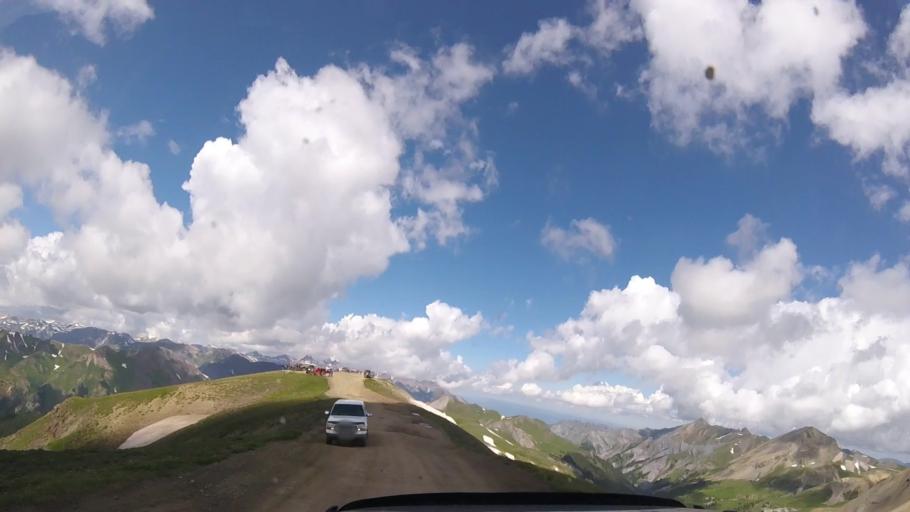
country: US
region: Colorado
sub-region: Ouray County
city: Ouray
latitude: 37.9696
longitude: -107.5924
